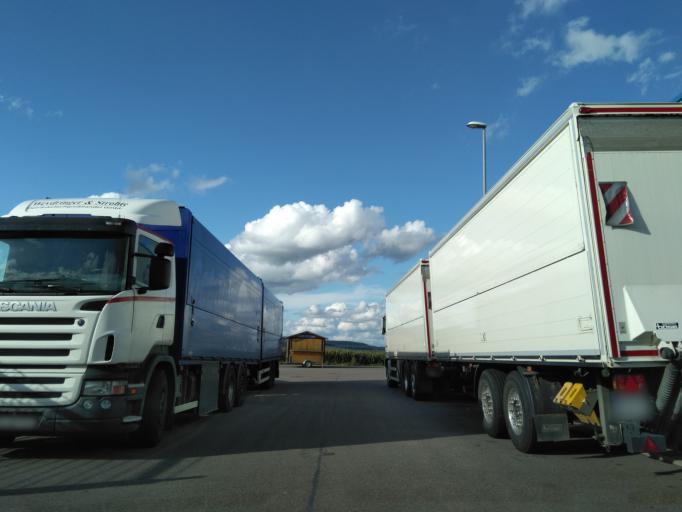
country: DE
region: Baden-Wuerttemberg
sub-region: Regierungsbezirk Stuttgart
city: Oberriexingen
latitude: 48.9517
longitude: 9.0513
